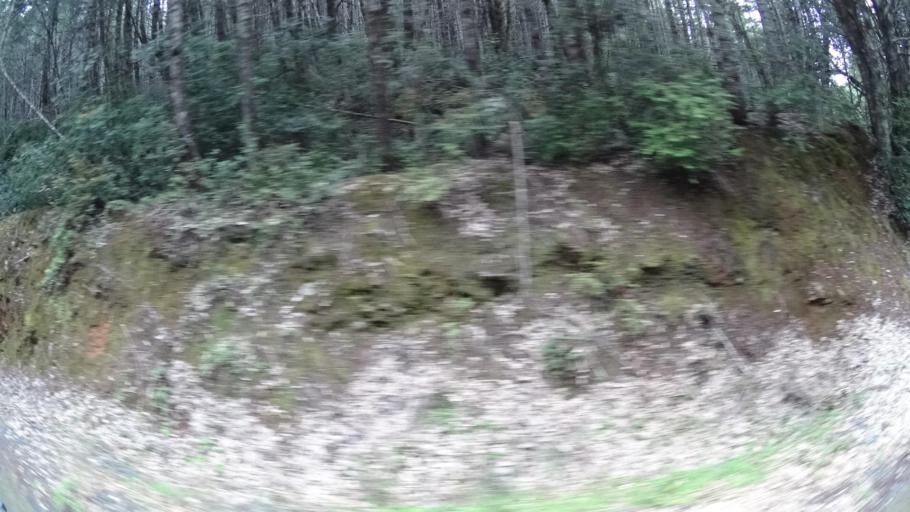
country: US
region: California
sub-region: Humboldt County
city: Willow Creek
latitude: 41.2006
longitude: -123.7672
